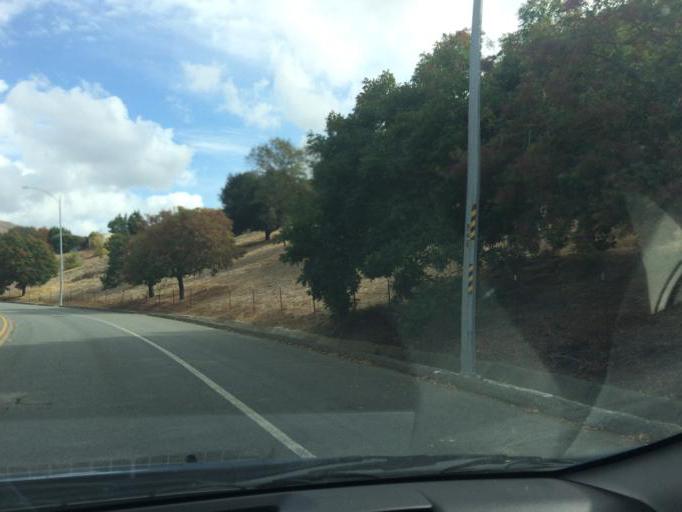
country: US
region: California
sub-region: Santa Clara County
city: Seven Trees
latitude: 37.2797
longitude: -121.7567
